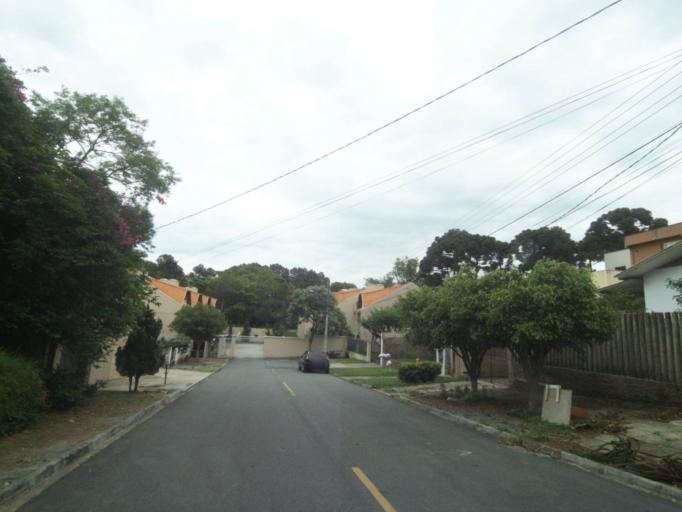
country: BR
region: Parana
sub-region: Curitiba
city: Curitiba
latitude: -25.3952
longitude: -49.2899
